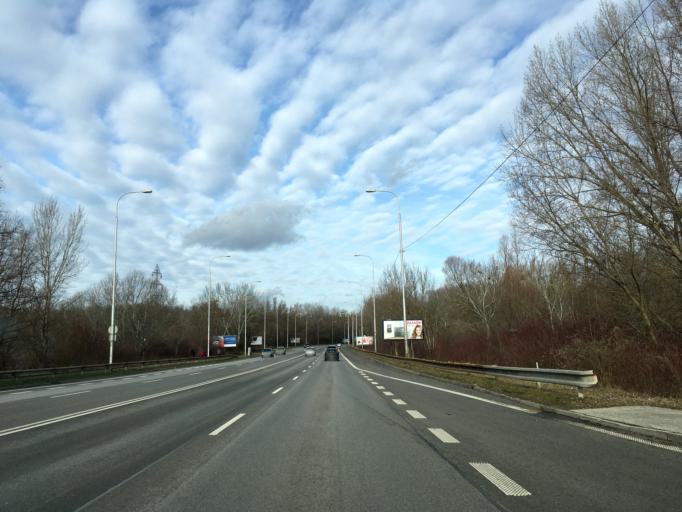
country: SK
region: Bratislavsky
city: Bratislava
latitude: 48.1012
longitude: 17.1214
